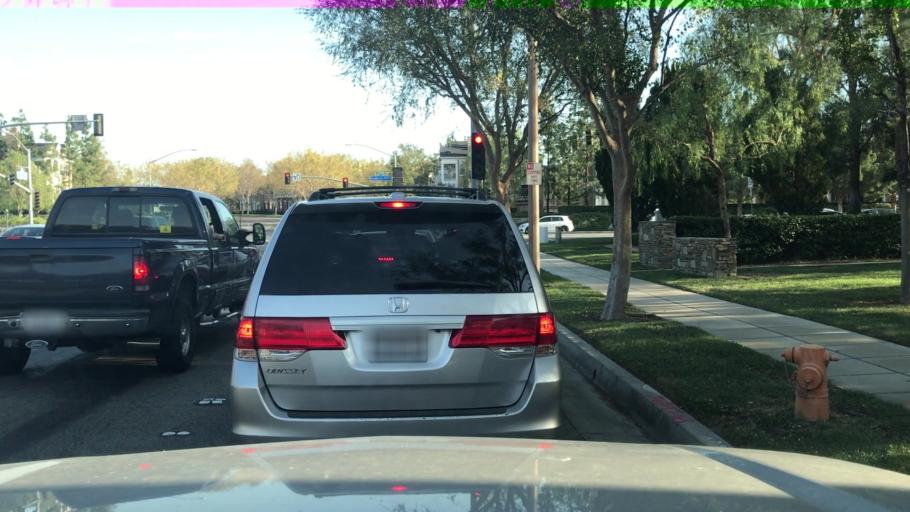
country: US
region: California
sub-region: Los Angeles County
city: Santa Clarita
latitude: 34.4278
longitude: -118.5618
